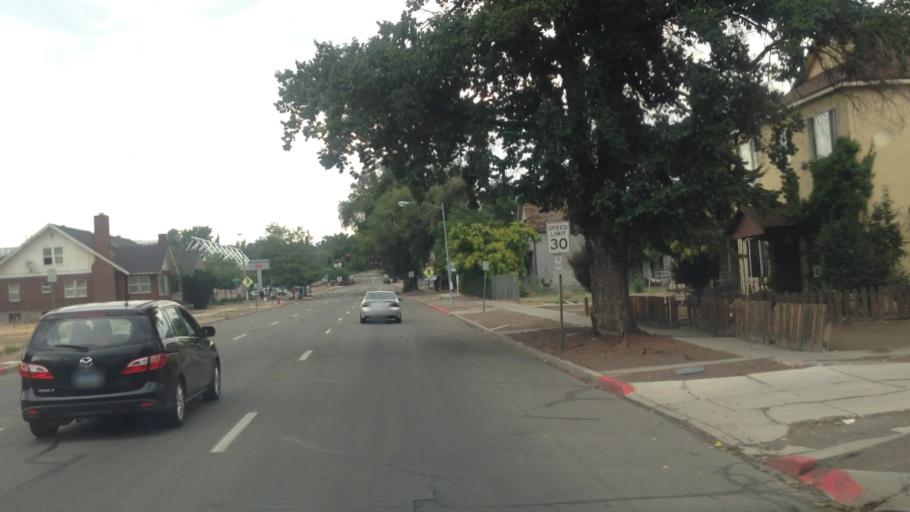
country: US
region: Nevada
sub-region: Washoe County
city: Reno
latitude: 39.5329
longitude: -119.8137
